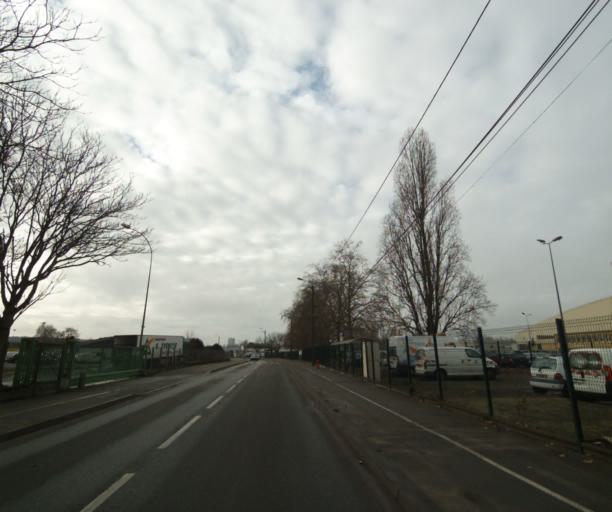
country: FR
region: Pays de la Loire
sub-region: Departement de la Sarthe
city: Allonnes
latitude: 47.9810
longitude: 0.1703
